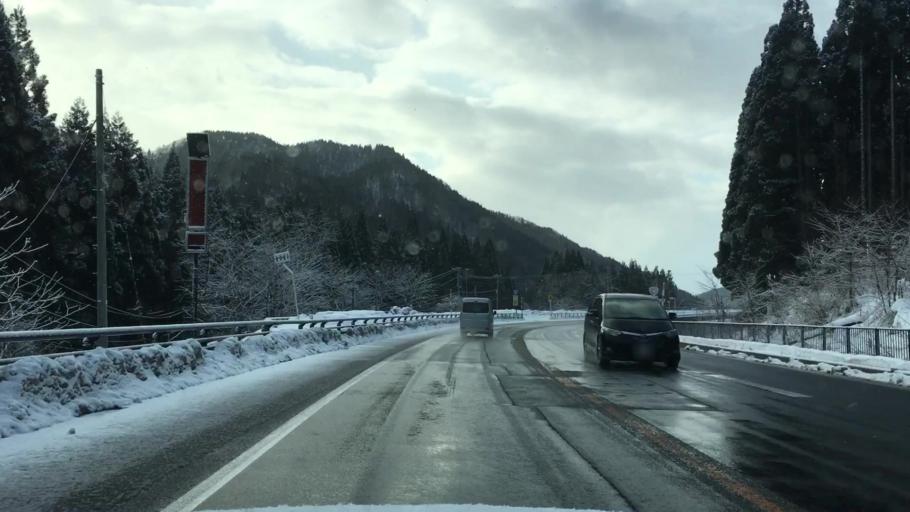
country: JP
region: Akita
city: Odate
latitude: 40.4101
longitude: 140.6120
